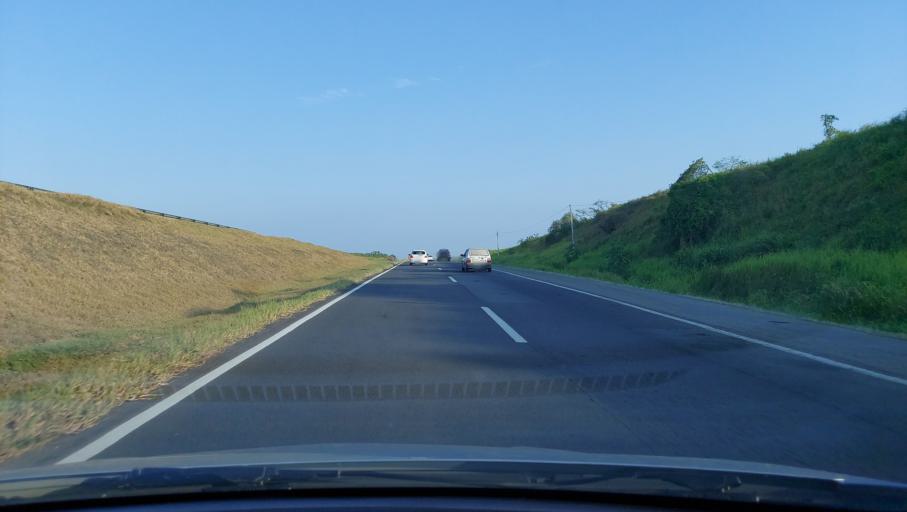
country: BR
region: Bahia
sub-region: Santo Amaro
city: Santo Amaro
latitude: -12.4859
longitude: -38.6625
